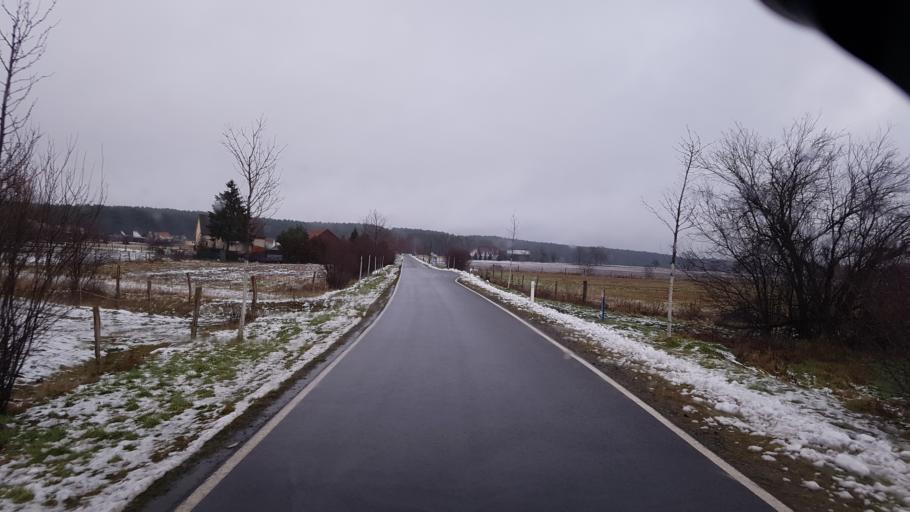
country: DE
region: Brandenburg
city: Neu Zauche
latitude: 51.9448
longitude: 14.1135
